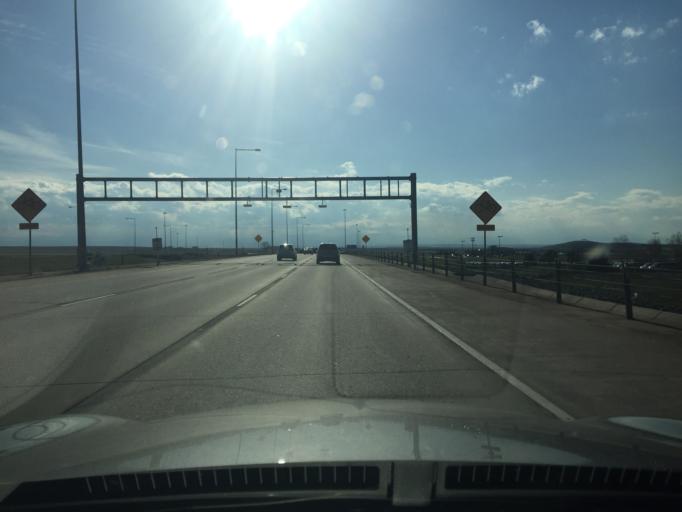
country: US
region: Colorado
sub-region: Adams County
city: Aurora
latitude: 39.8345
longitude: -104.7124
